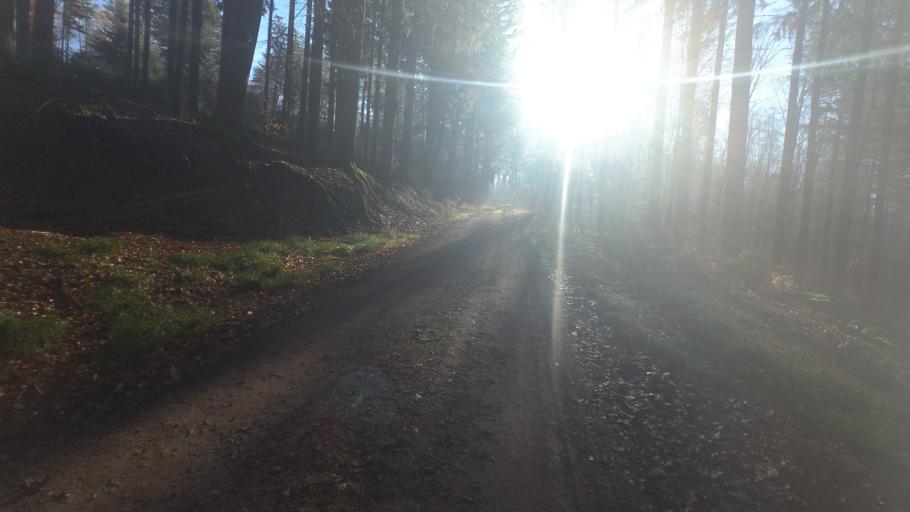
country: DE
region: Baden-Wuerttemberg
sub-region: Karlsruhe Region
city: Heddesbach
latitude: 49.4918
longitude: 8.8135
